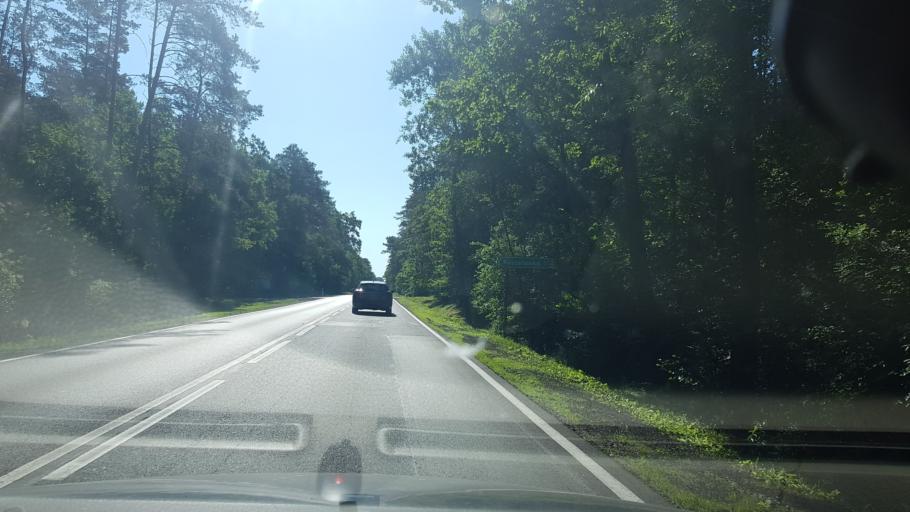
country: PL
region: Masovian Voivodeship
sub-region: Powiat wyszkowski
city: Branszczyk
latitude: 52.5544
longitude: 21.6018
